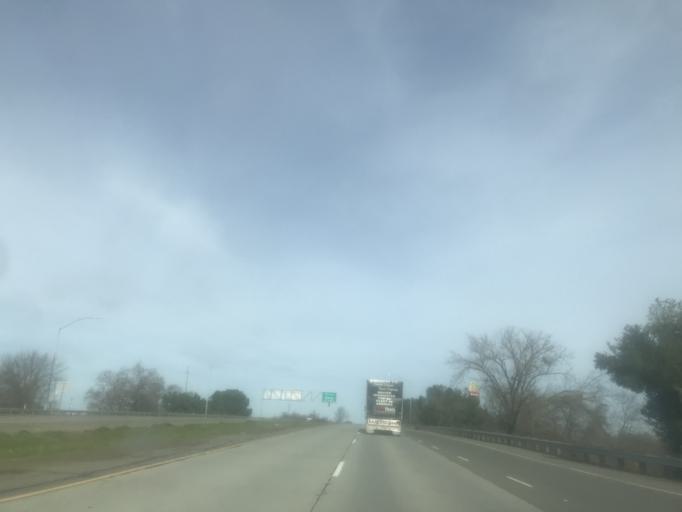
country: US
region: California
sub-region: Yolo County
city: Woodland
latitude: 38.6754
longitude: -121.7510
